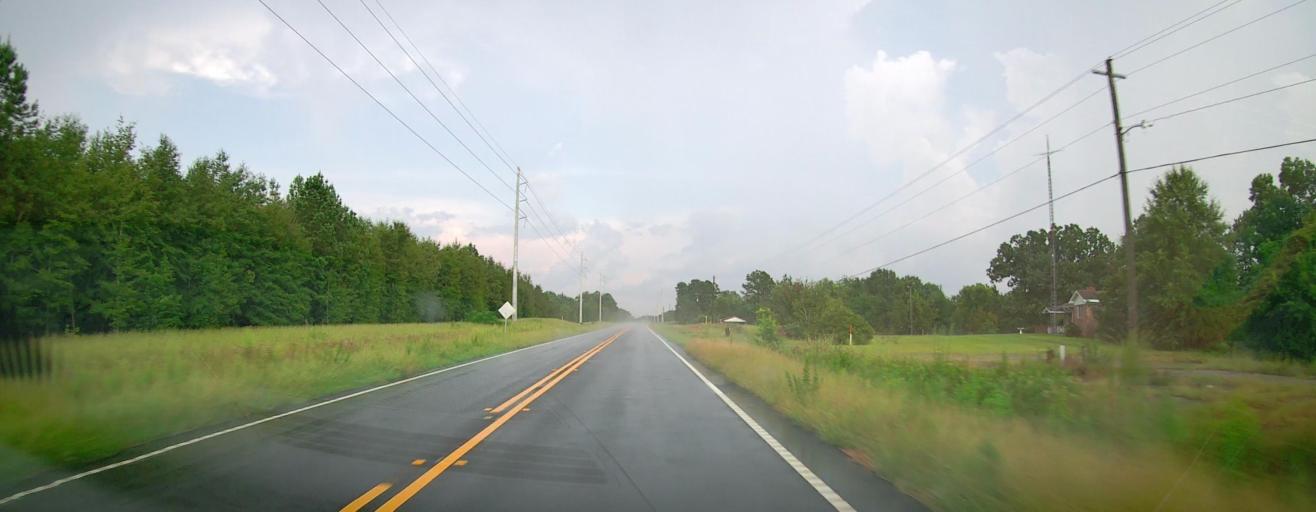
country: US
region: Georgia
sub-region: Twiggs County
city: Jeffersonville
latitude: 32.5783
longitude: -83.2084
